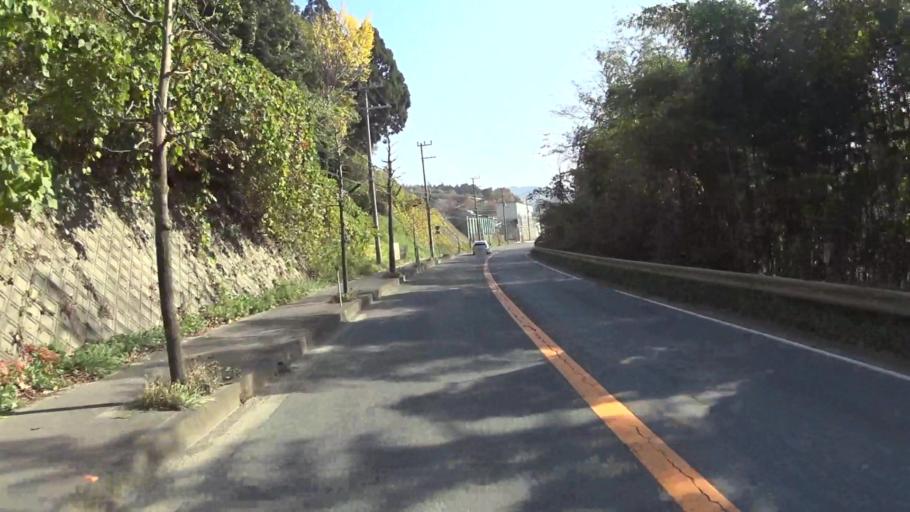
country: JP
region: Kyoto
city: Maizuru
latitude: 35.4294
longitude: 135.2323
